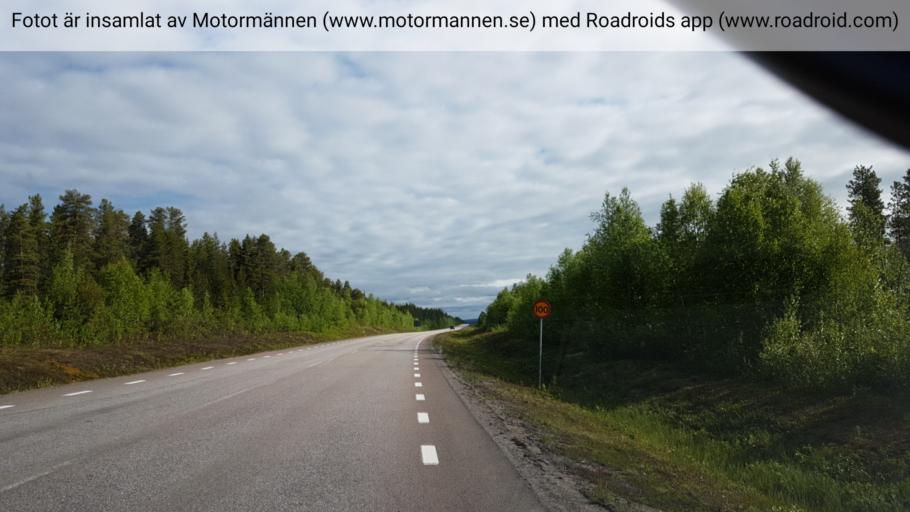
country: SE
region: Norrbotten
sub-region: Gallivare Kommun
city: Malmberget
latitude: 67.4911
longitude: 21.1209
